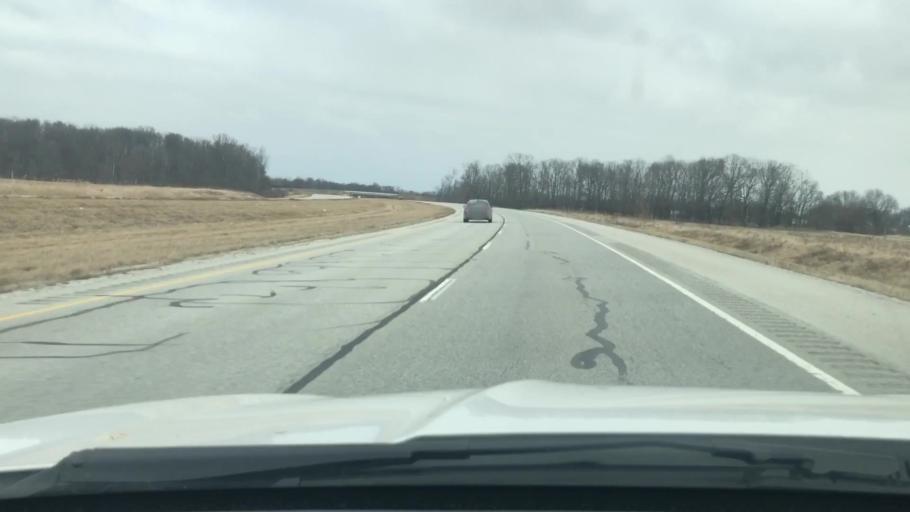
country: US
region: Indiana
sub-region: Carroll County
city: Delphi
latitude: 40.6368
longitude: -86.5847
